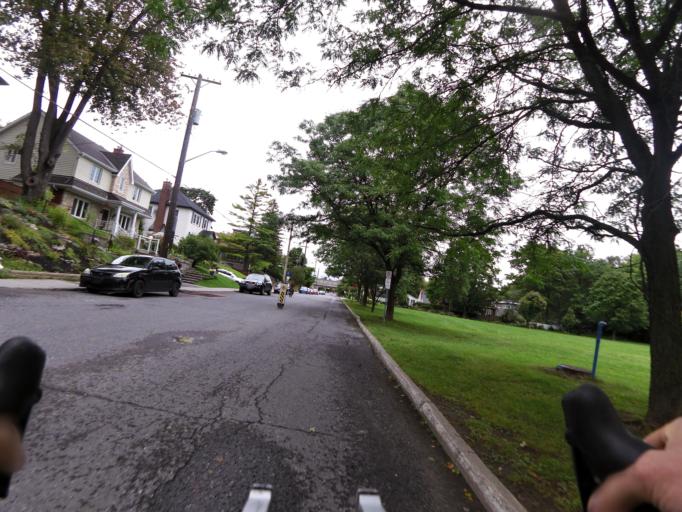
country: CA
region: Ontario
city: Ottawa
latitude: 45.3980
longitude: -75.7195
